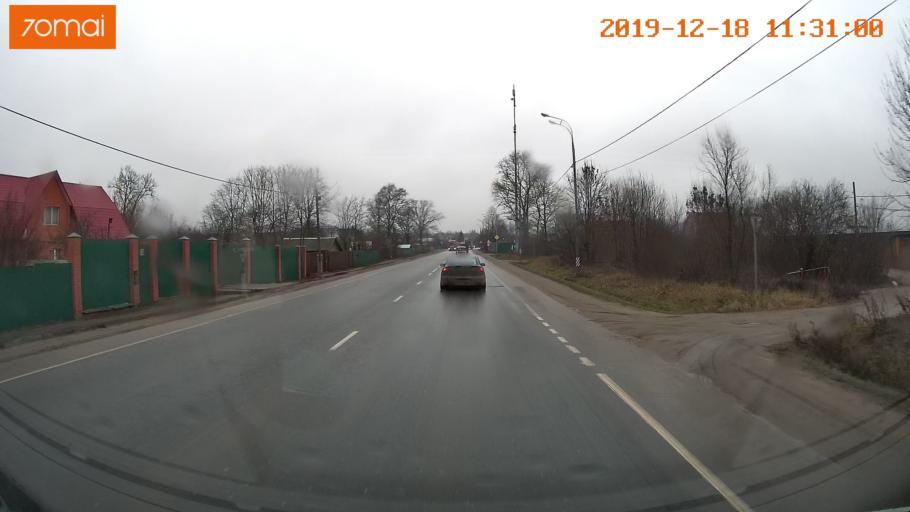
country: RU
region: Moskovskaya
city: Bol'shiye Vyazemy
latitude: 55.6626
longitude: 36.9652
